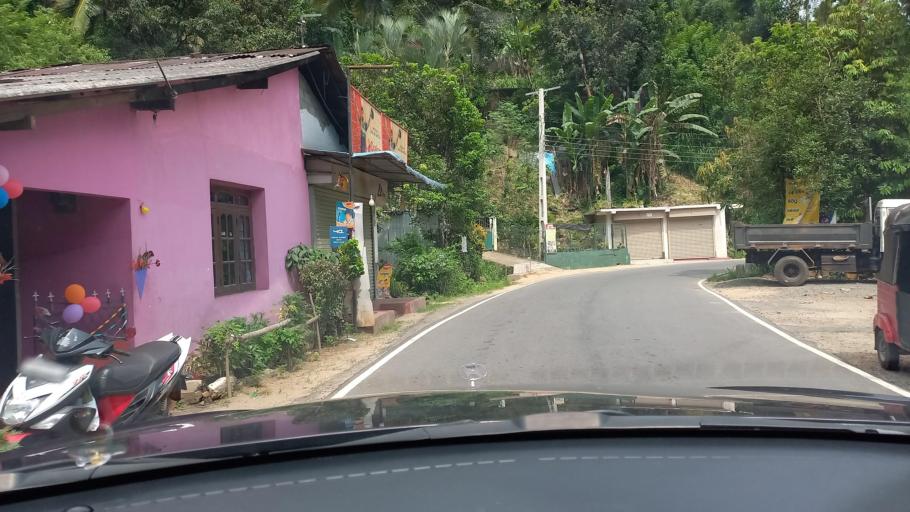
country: LK
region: Central
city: Gampola
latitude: 7.2190
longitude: 80.6140
